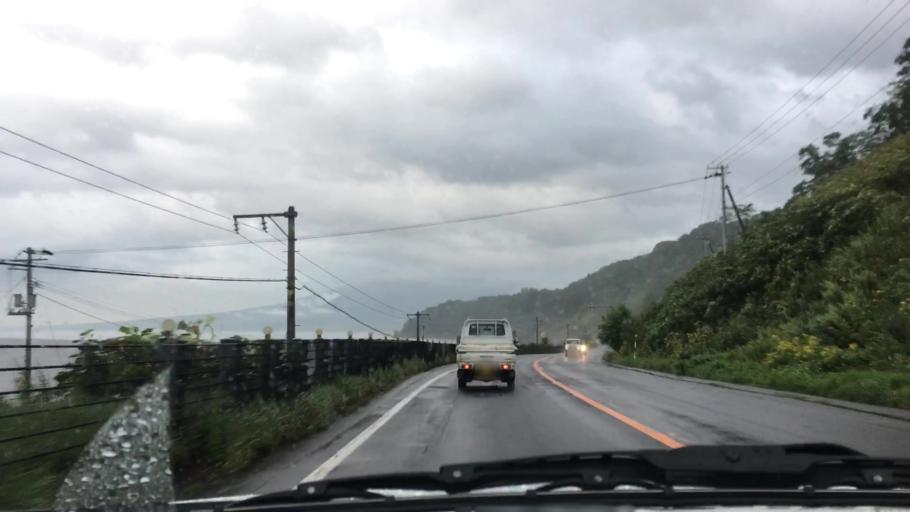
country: JP
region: Hokkaido
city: Nanae
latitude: 42.1272
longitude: 140.5167
